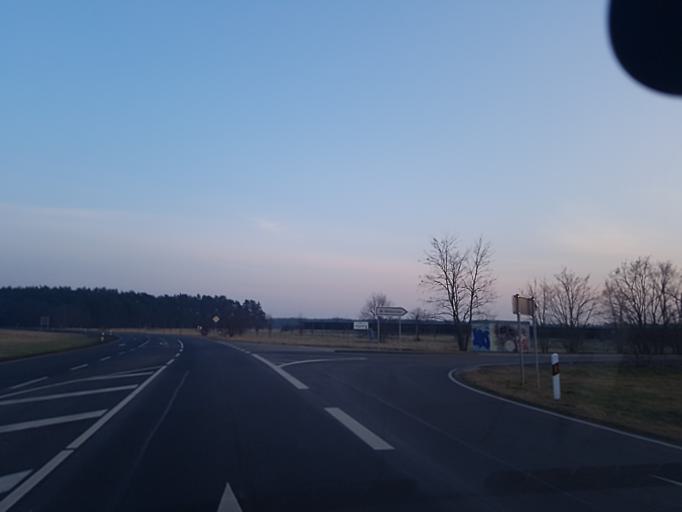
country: DE
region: Saxony-Anhalt
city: Jessen
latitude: 51.8048
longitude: 12.9221
